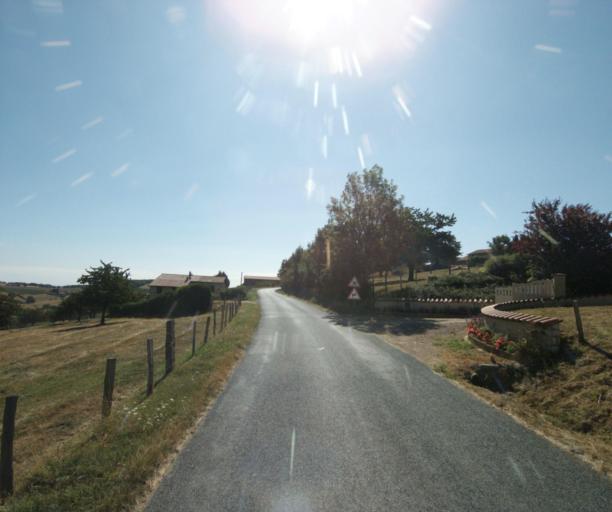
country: FR
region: Rhone-Alpes
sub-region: Departement du Rhone
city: Saint-Romain-de-Popey
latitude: 45.8249
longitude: 4.5319
